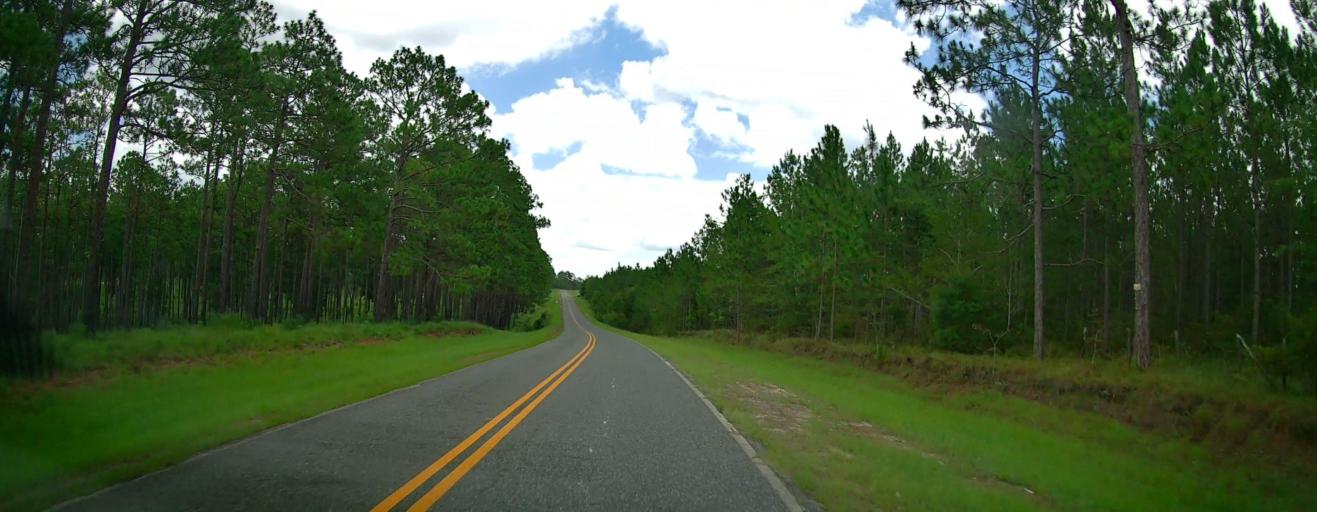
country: US
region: Georgia
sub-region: Turner County
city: Ashburn
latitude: 31.6982
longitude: -83.4953
